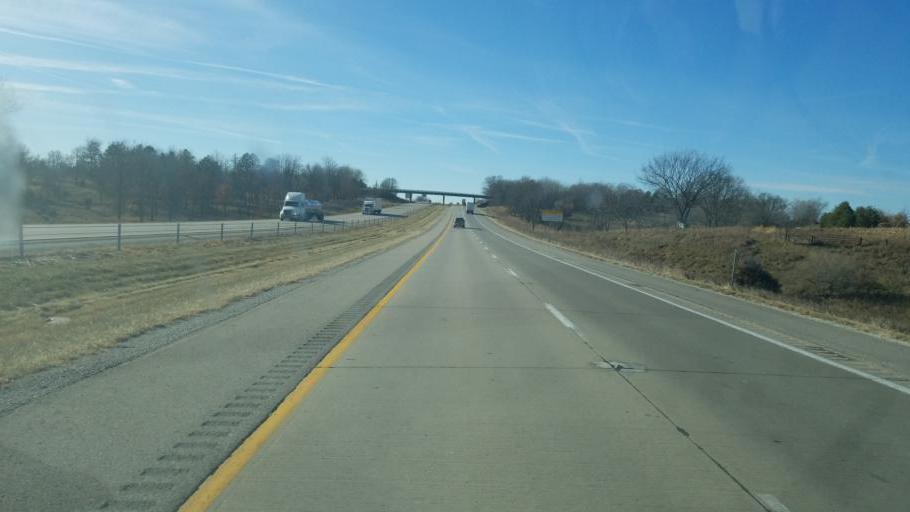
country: US
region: Iowa
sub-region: Dallas County
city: De Soto
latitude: 41.5371
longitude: -94.0307
